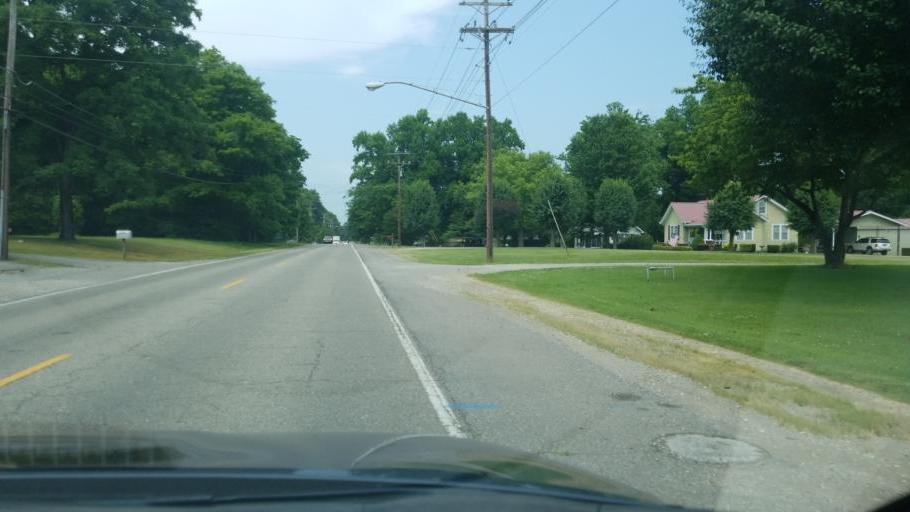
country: US
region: Tennessee
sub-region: Humphreys County
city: Waverly
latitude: 36.0830
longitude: -87.8127
